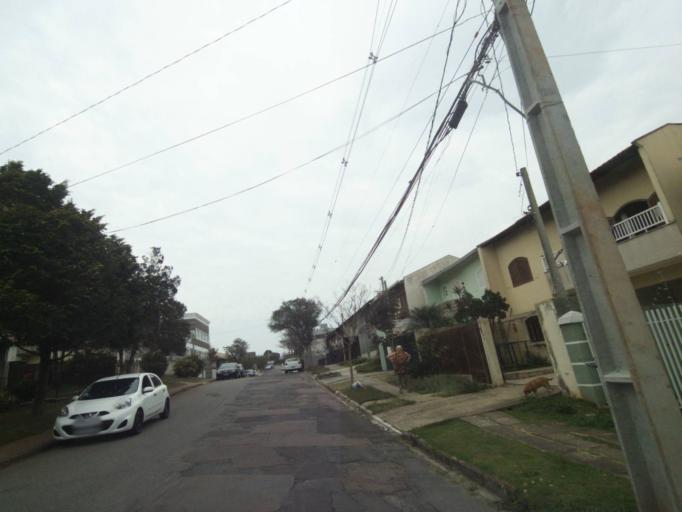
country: BR
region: Parana
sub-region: Curitiba
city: Curitiba
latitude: -25.4616
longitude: -49.3030
